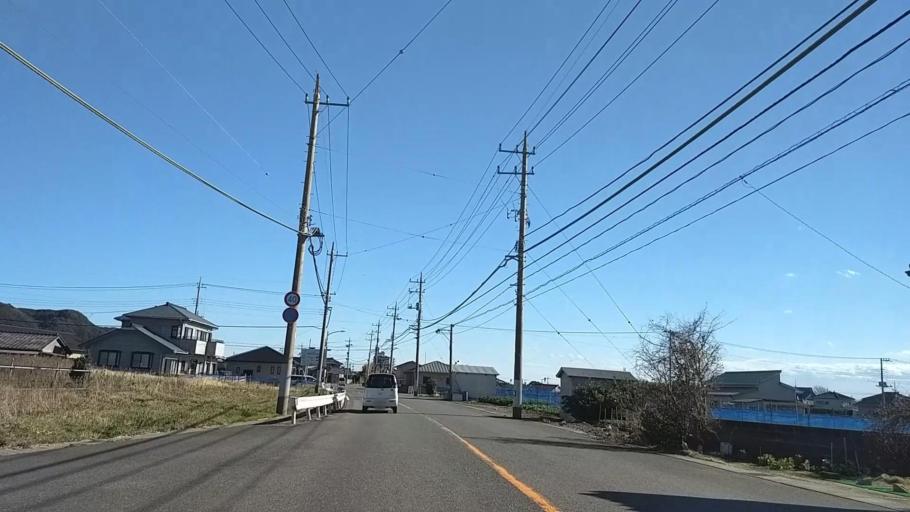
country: JP
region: Chiba
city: Tateyama
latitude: 34.9074
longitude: 139.8858
